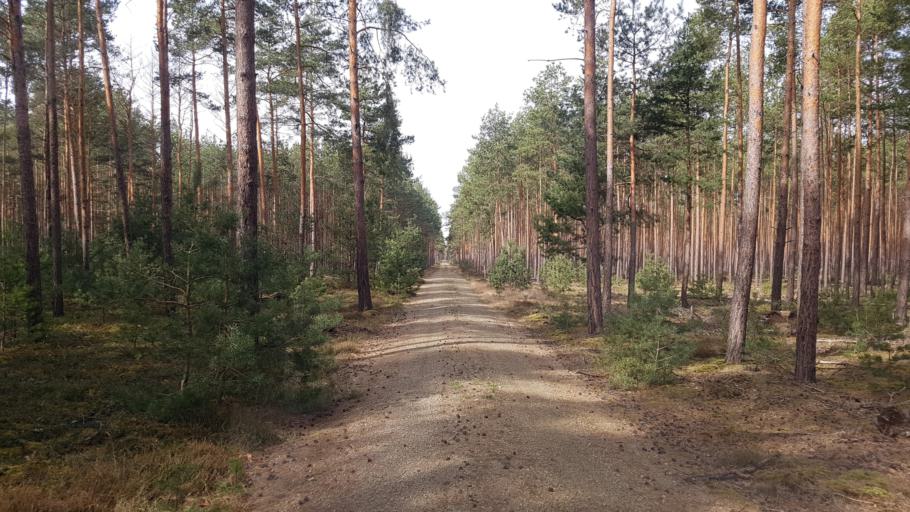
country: DE
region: Brandenburg
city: Elsterwerda
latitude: 51.5003
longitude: 13.4634
